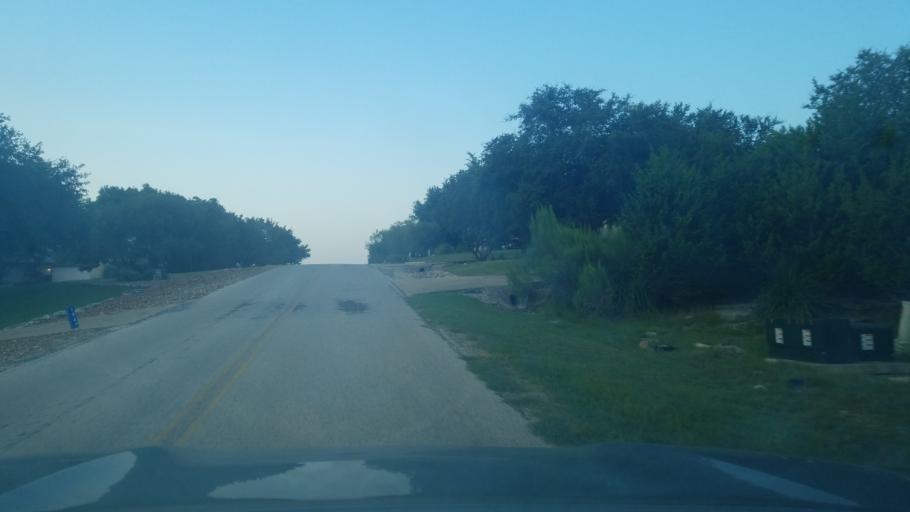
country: US
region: Texas
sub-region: Comal County
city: Bulverde
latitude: 29.8233
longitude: -98.4029
